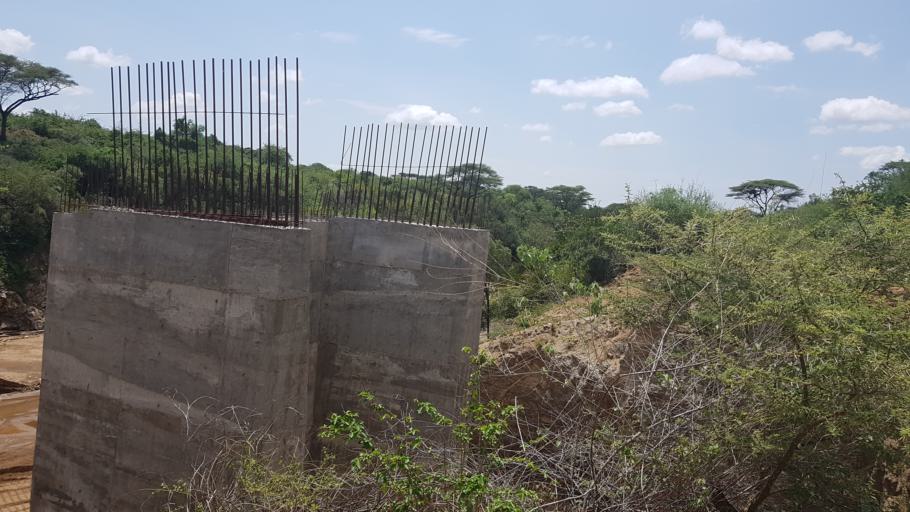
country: ET
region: Southern Nations, Nationalities, and People's Region
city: Turmi
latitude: 5.0577
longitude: 36.2697
